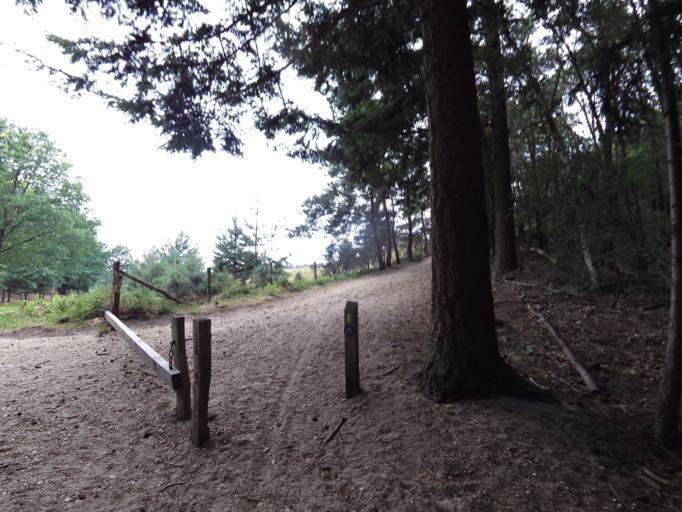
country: NL
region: North Brabant
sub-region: Gemeente Cuijk
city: Cuijk
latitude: 51.7653
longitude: 5.8906
